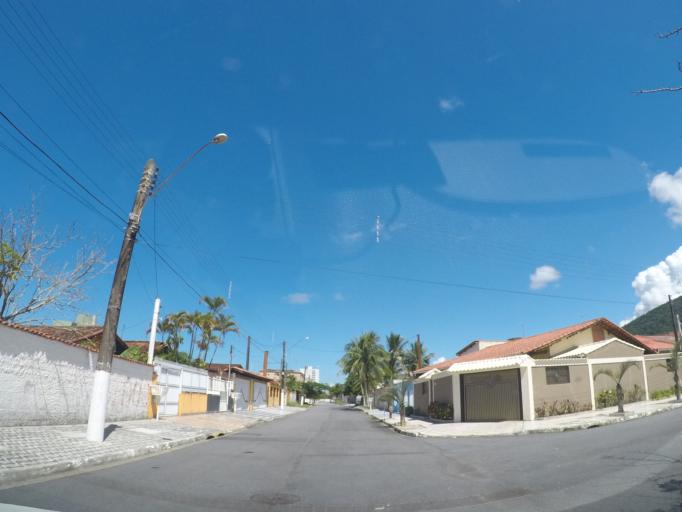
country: BR
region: Sao Paulo
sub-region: Mongagua
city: Mongagua
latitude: -24.0811
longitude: -46.5922
